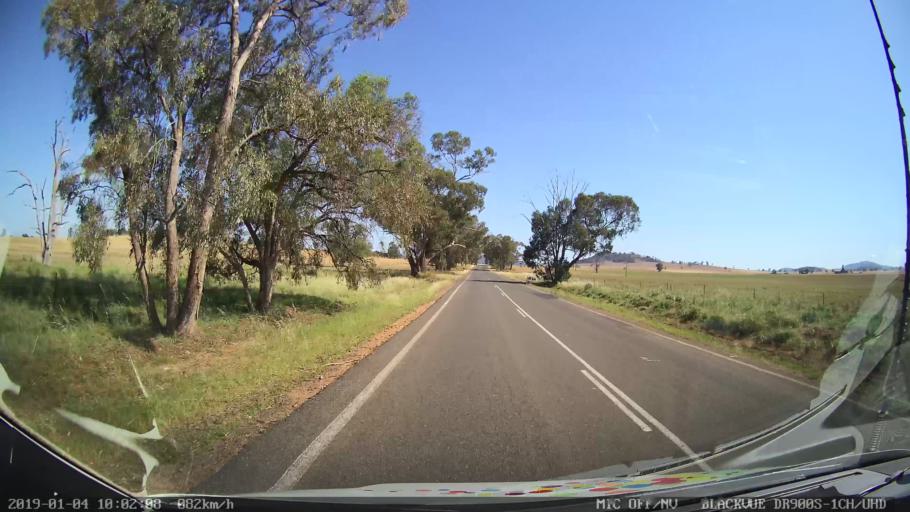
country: AU
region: New South Wales
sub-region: Cabonne
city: Canowindra
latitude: -33.4800
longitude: 148.3660
